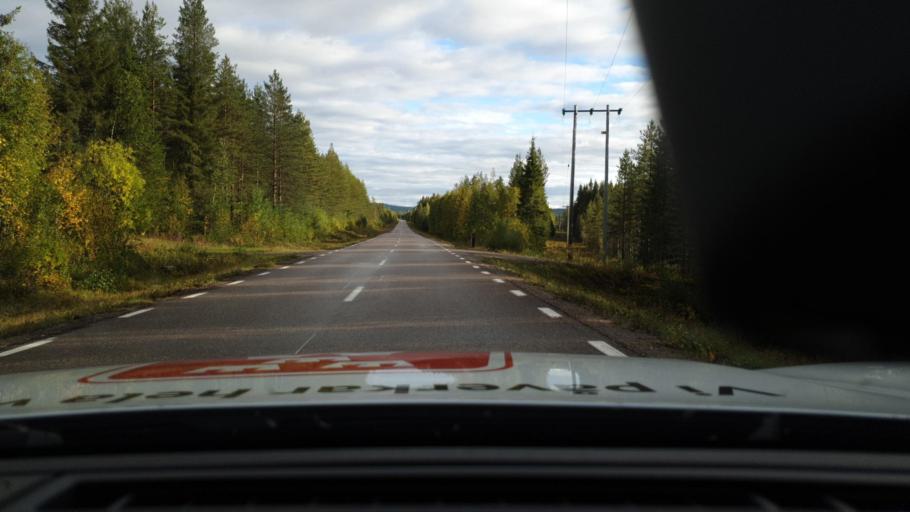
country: SE
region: Norrbotten
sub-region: Overkalix Kommun
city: OEverkalix
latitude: 66.6393
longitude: 22.7238
